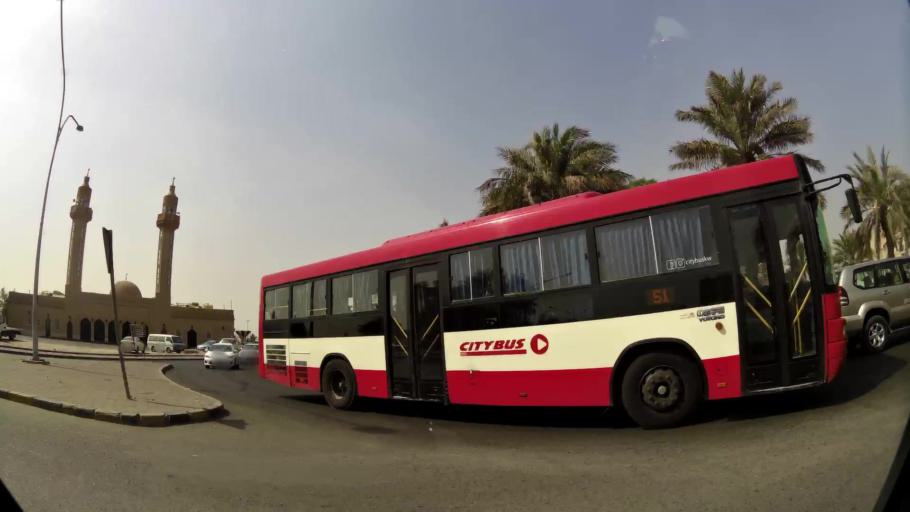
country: KW
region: Al Farwaniyah
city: Al Farwaniyah
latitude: 29.2545
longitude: 47.9243
